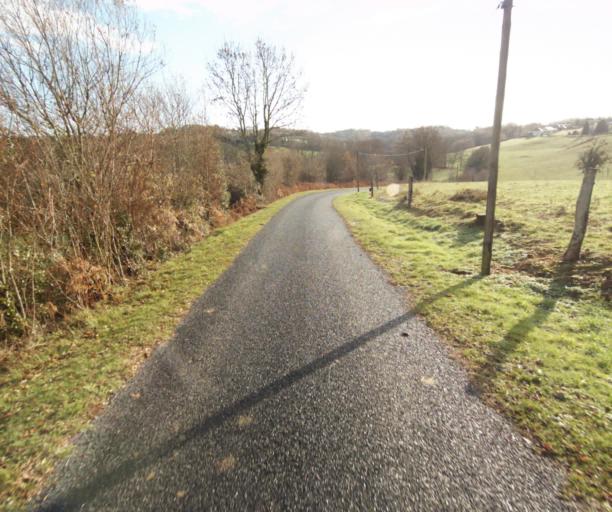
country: FR
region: Limousin
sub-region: Departement de la Correze
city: Sainte-Fereole
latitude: 45.2529
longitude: 1.6045
